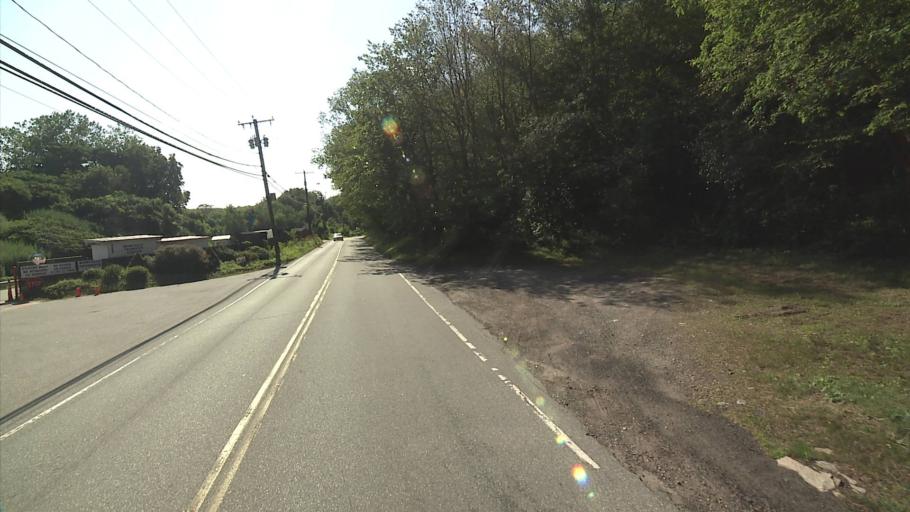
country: US
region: Connecticut
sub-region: New London County
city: Montville Center
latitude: 41.4634
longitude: -72.1573
